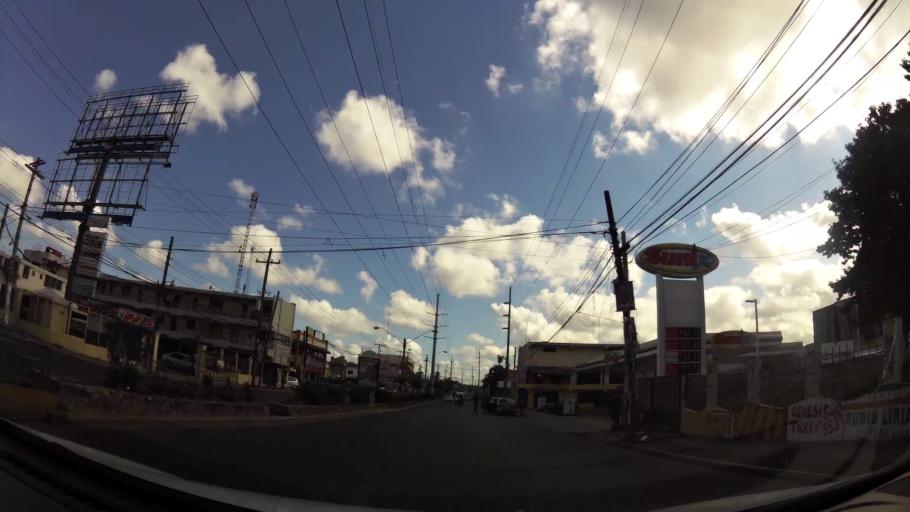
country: DO
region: Santo Domingo
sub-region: Santo Domingo
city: Santo Domingo Este
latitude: 18.5070
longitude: -69.8543
